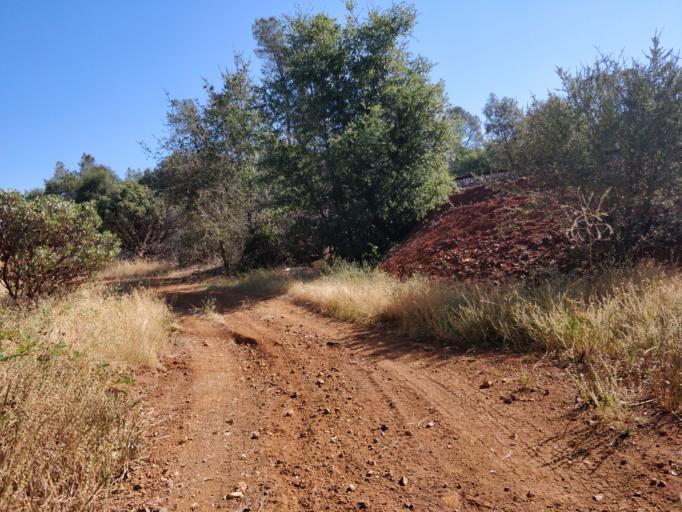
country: US
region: California
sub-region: Shasta County
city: Central Valley (historical)
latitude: 40.6673
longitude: -122.3945
